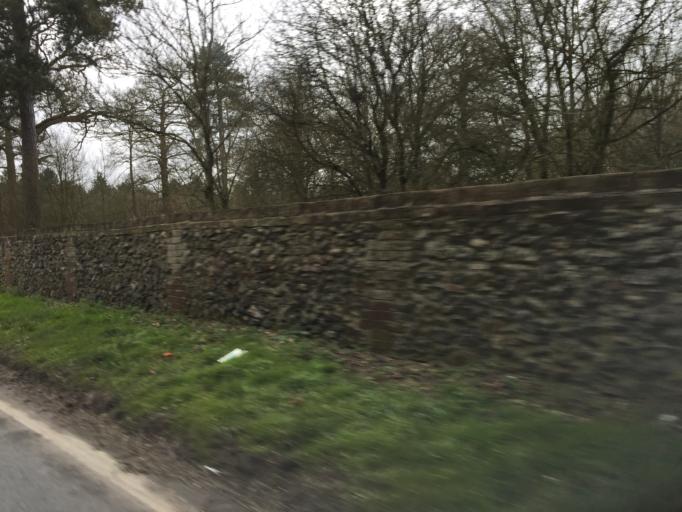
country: GB
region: England
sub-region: West Berkshire
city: Theale
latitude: 51.4359
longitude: -1.0922
